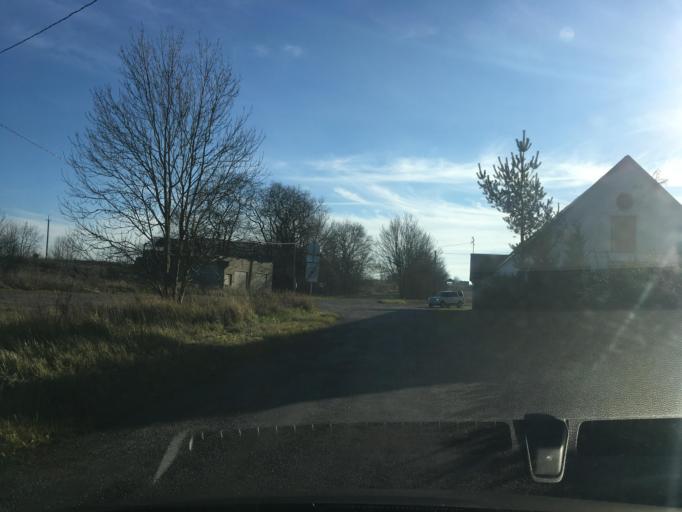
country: EE
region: Harju
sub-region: Maardu linn
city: Maardu
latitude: 59.4884
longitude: 25.0777
